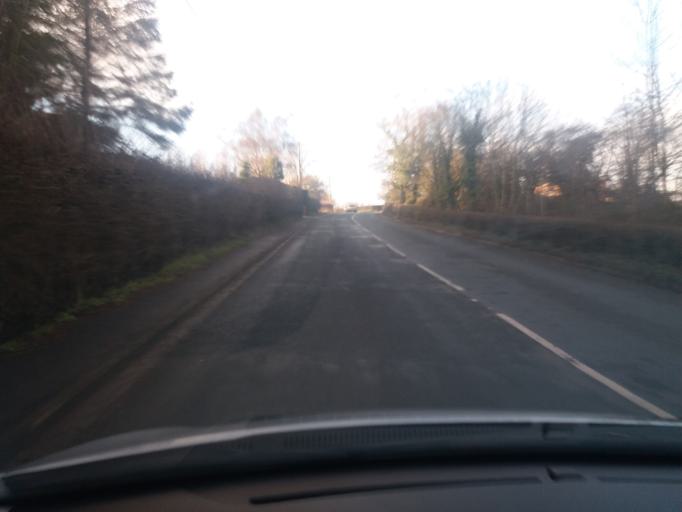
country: GB
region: England
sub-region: Lancashire
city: Euxton
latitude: 53.6621
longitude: -2.7076
